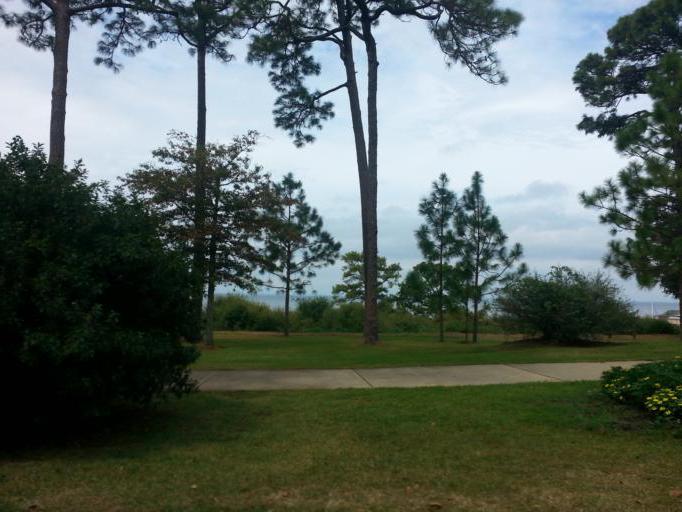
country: US
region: Alabama
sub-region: Baldwin County
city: Fairhope
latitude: 30.5223
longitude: -87.9120
